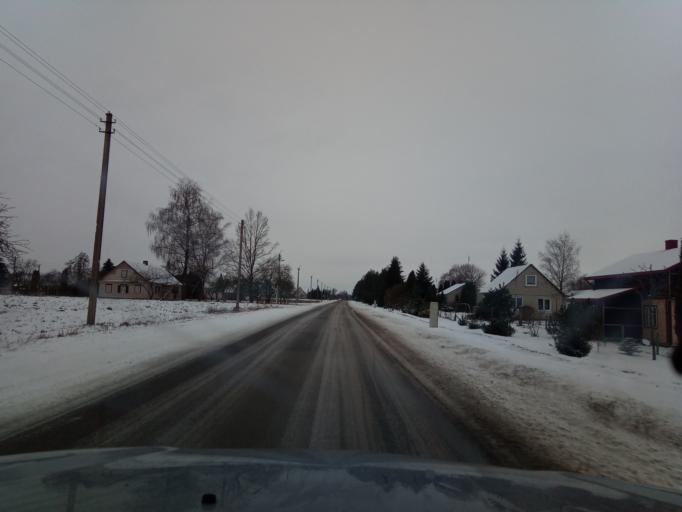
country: LT
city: Ramygala
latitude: 55.4934
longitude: 24.4891
